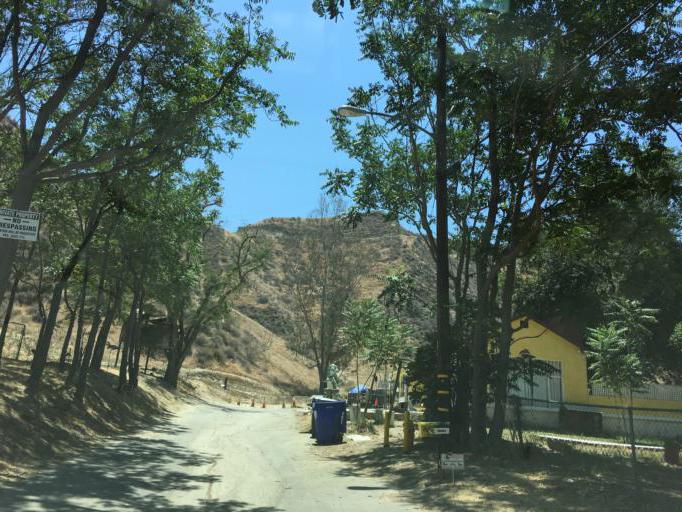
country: US
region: California
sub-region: Los Angeles County
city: Val Verde
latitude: 34.4459
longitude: -118.6709
